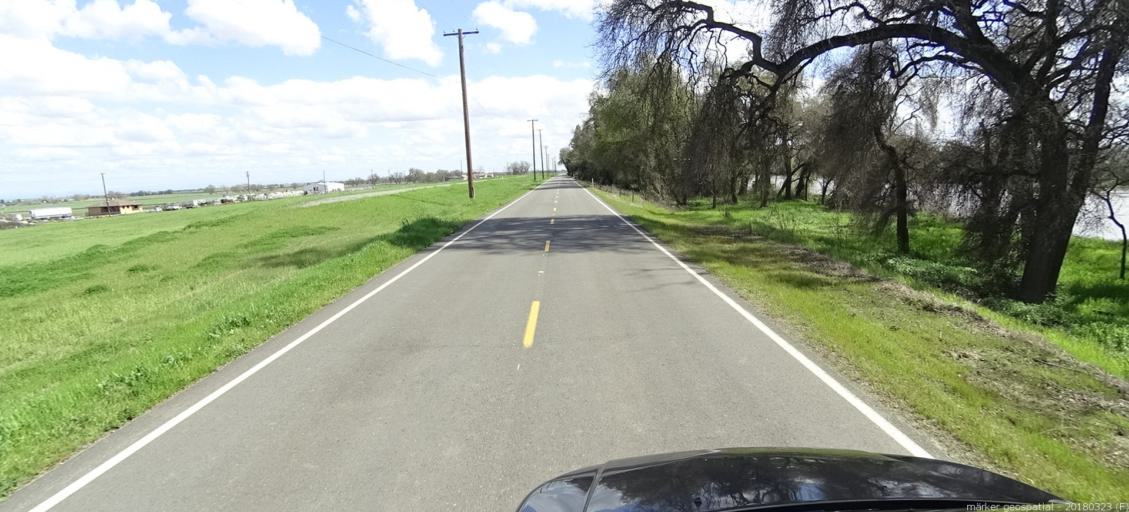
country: US
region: California
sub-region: Yolo County
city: West Sacramento
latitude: 38.6695
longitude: -121.6193
